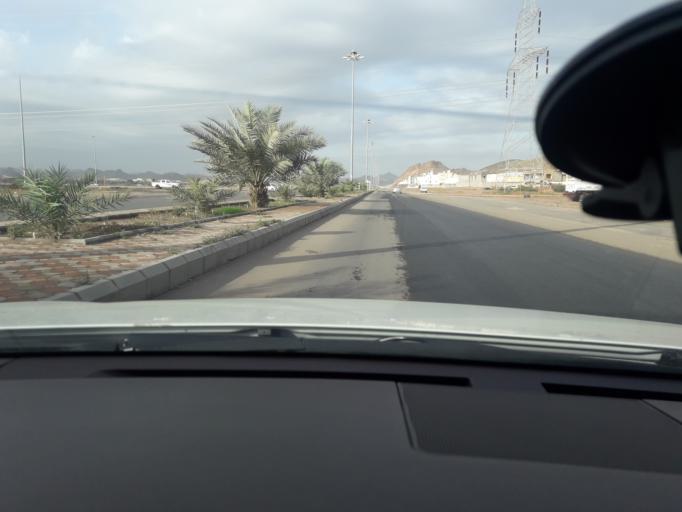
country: SA
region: Al Madinah al Munawwarah
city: Sultanah
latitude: 24.4675
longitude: 39.4888
